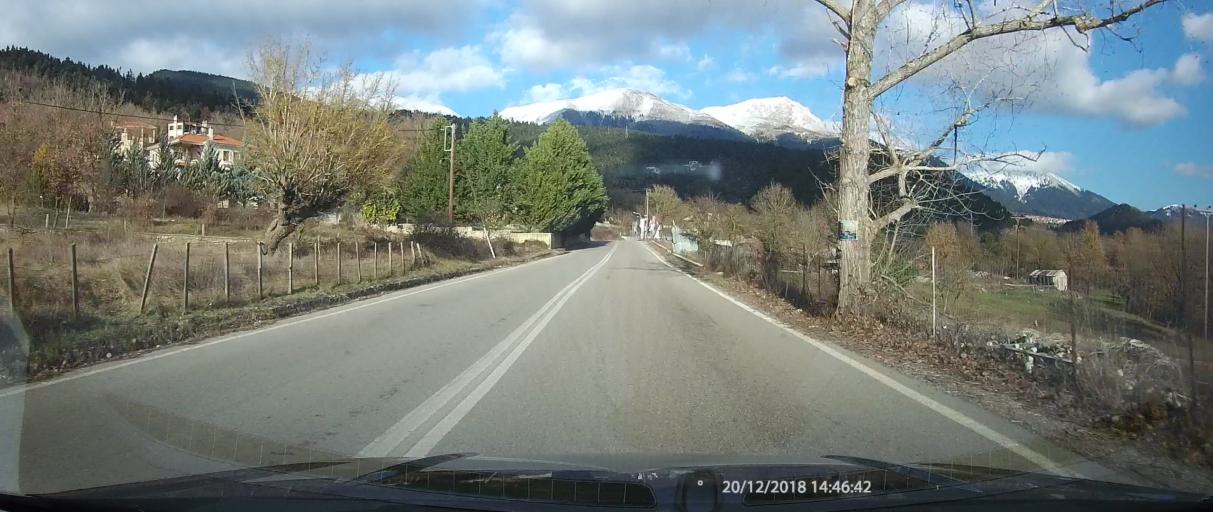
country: GR
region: Central Greece
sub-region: Nomos Evrytanias
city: Karpenisi
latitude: 38.8983
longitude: 21.7701
